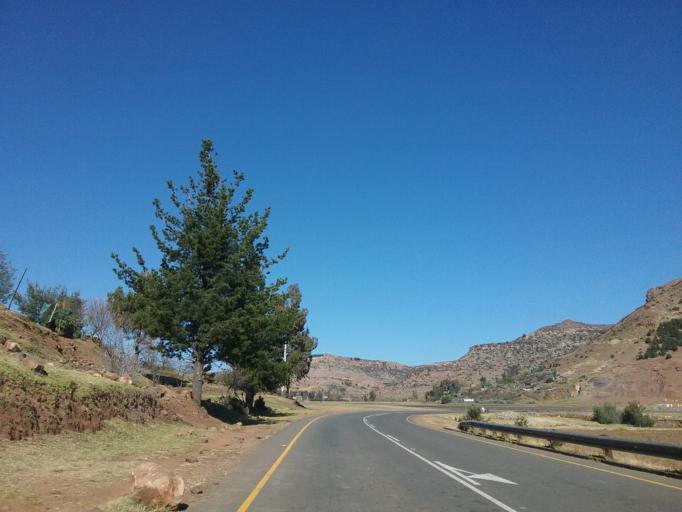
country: LS
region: Maseru
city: Nako
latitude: -29.5130
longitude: 27.6381
